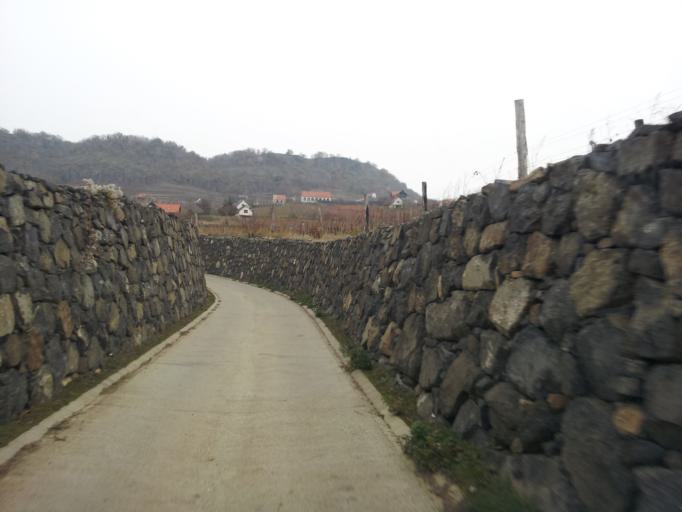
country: HU
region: Veszprem
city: Devecser
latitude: 47.1365
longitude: 17.3701
